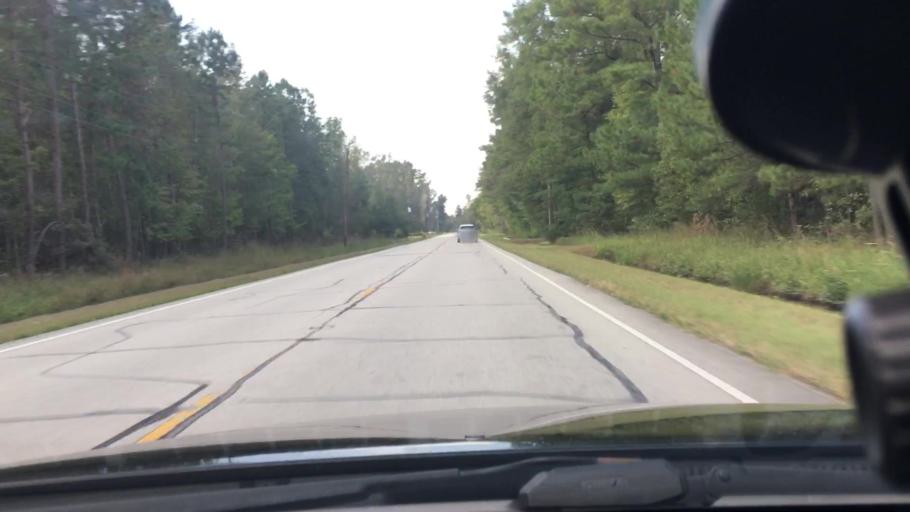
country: US
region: North Carolina
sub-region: Craven County
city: Vanceboro
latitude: 35.3246
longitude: -77.1677
